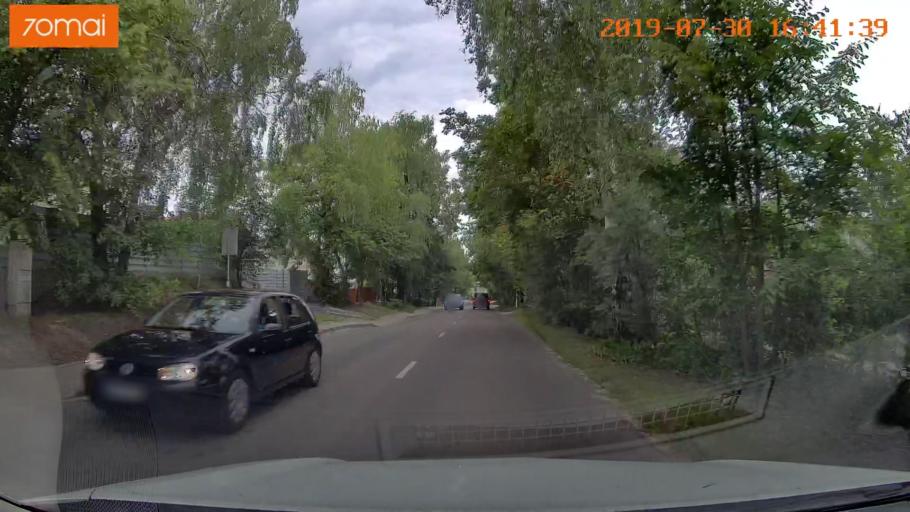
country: LT
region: Vilnius County
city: Rasos
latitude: 54.7127
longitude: 25.3533
